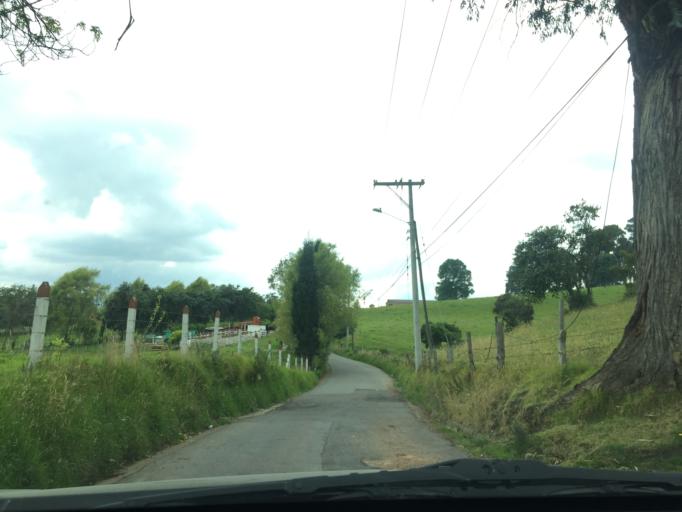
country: CO
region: Cundinamarca
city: Zipaquira
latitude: 5.0453
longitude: -74.0009
